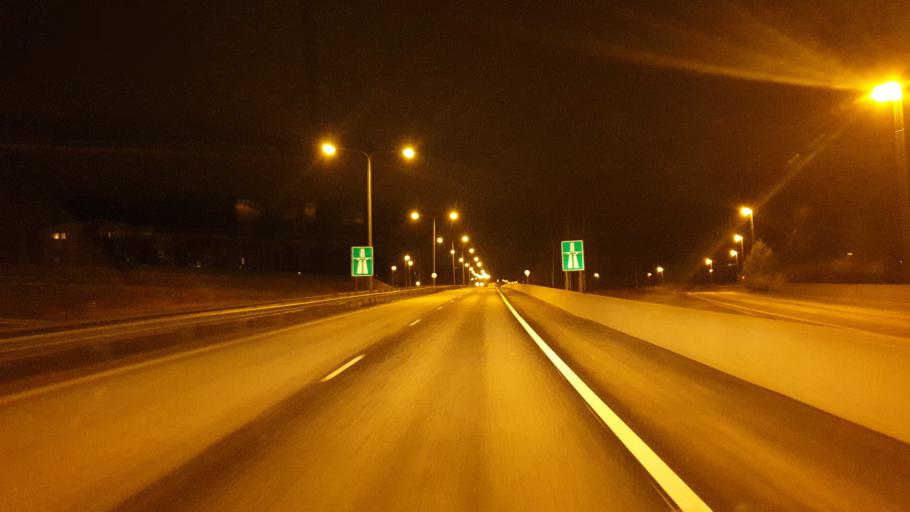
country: FI
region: Central Finland
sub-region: Jyvaeskylae
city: Jyvaeskylae
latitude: 62.2683
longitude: 25.7310
